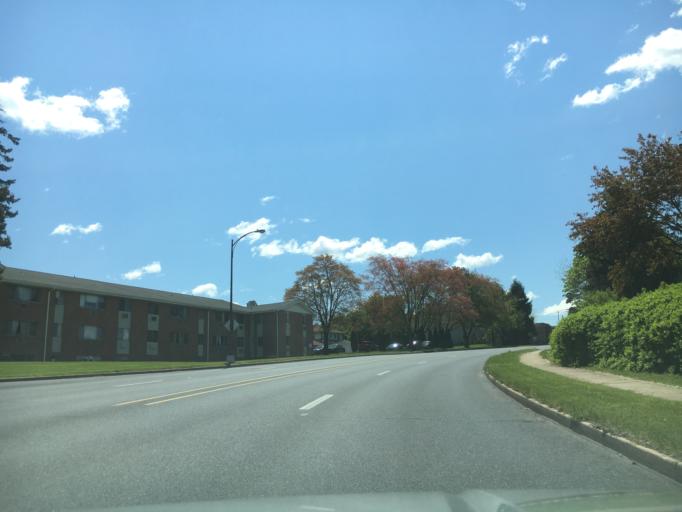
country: US
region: Pennsylvania
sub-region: Lehigh County
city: Allentown
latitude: 40.5901
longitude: -75.4799
